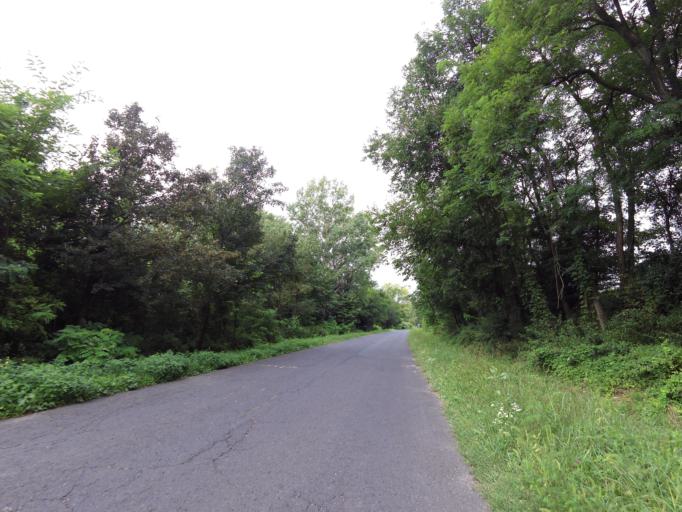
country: HU
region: Veszprem
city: Tapolca
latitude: 46.8422
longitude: 17.3557
